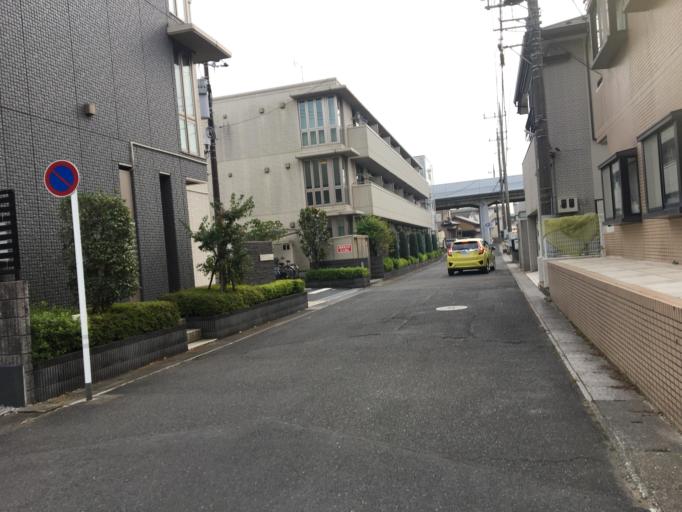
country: JP
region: Saitama
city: Yoshikawa
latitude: 35.8774
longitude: 139.8417
